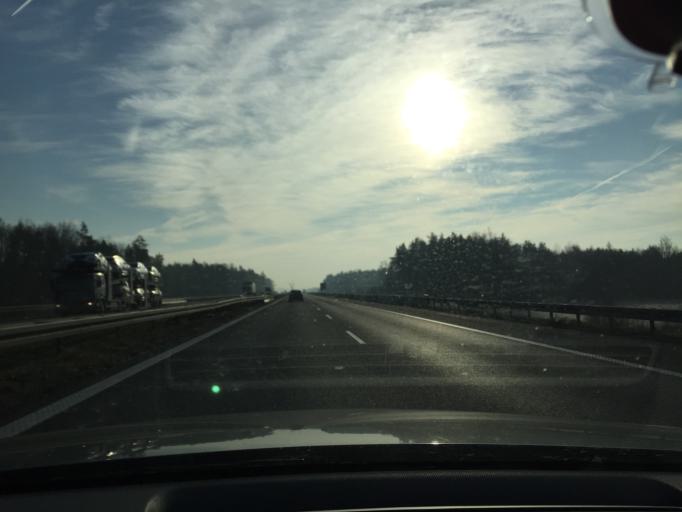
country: PL
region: Silesian Voivodeship
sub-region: Powiat gliwicki
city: Sosnicowice
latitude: 50.3234
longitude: 18.5478
